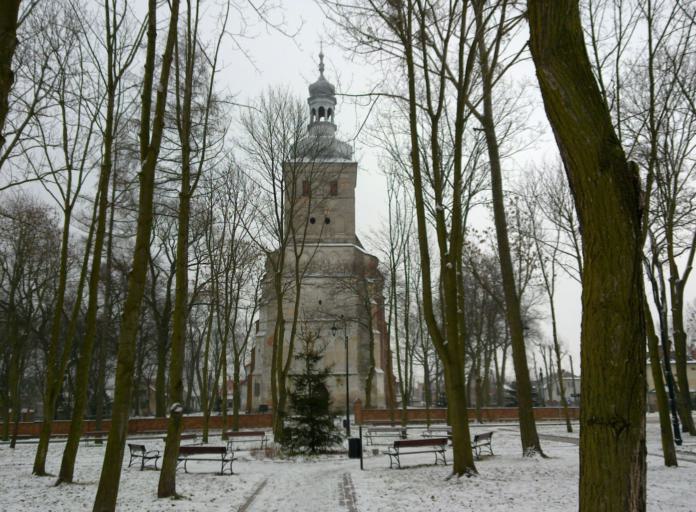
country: PL
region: Kujawsko-Pomorskie
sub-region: Powiat aleksandrowski
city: Raciazek
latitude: 52.8572
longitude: 18.8110
